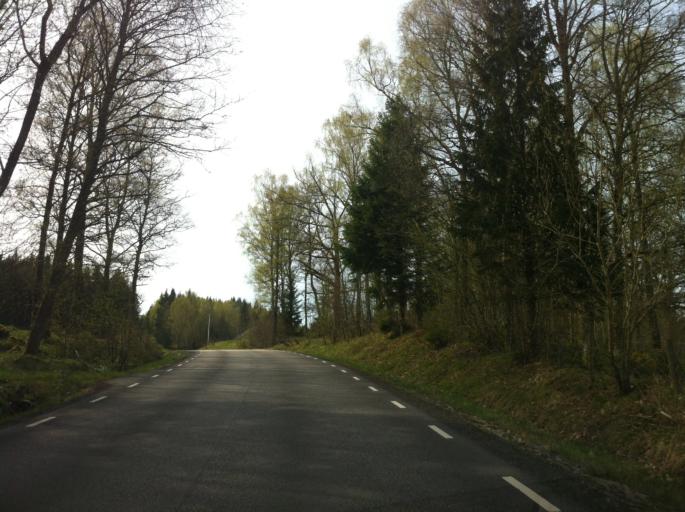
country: SE
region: Vaestra Goetaland
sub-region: Marks Kommun
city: Fritsla
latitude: 57.4018
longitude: 12.8522
